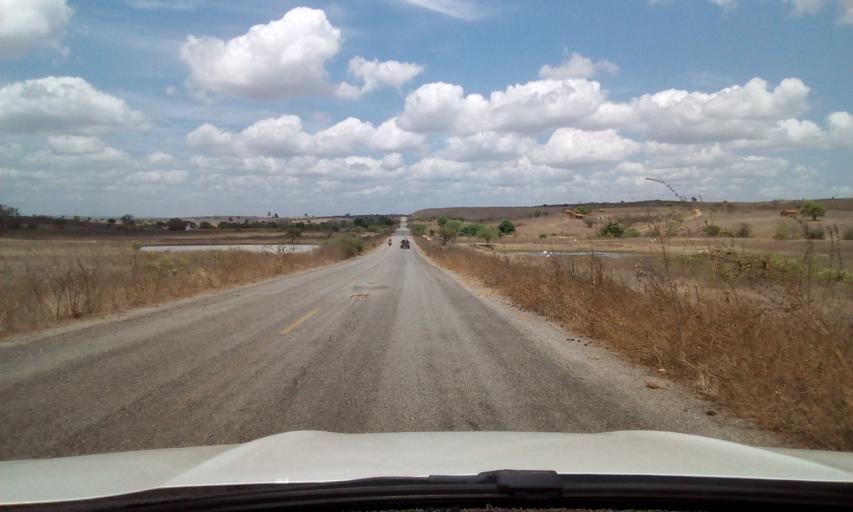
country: BR
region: Paraiba
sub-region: Gurinhem
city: Gurinhem
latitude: -7.0980
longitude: -35.4449
